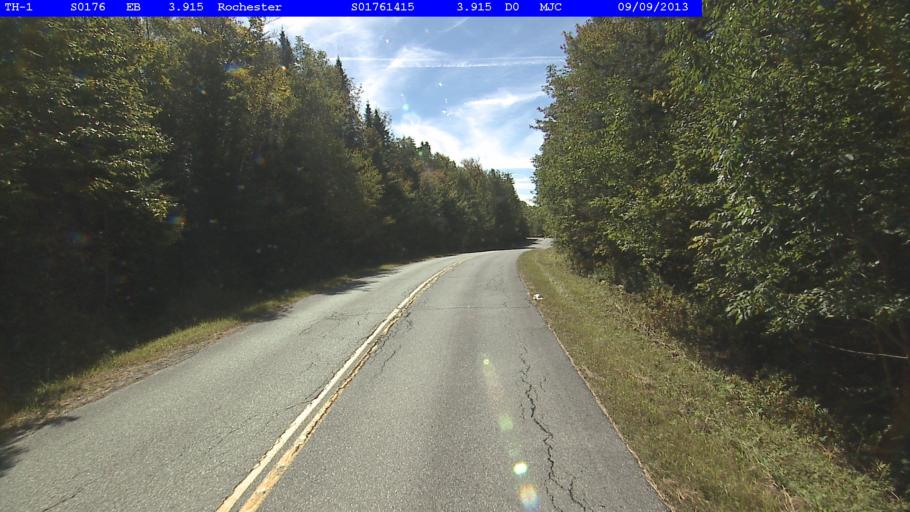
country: US
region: Vermont
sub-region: Orange County
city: Randolph
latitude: 43.8517
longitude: -72.7515
